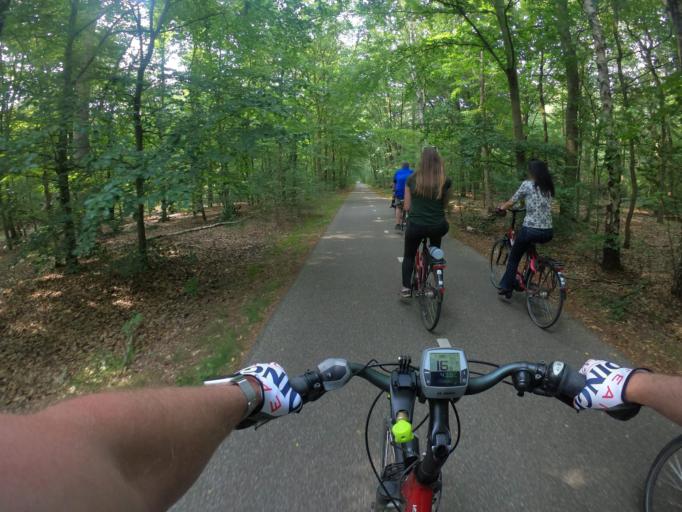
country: NL
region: Gelderland
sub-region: Gemeente Nijmegen
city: Nijmegen
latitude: 51.8004
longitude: 5.8592
